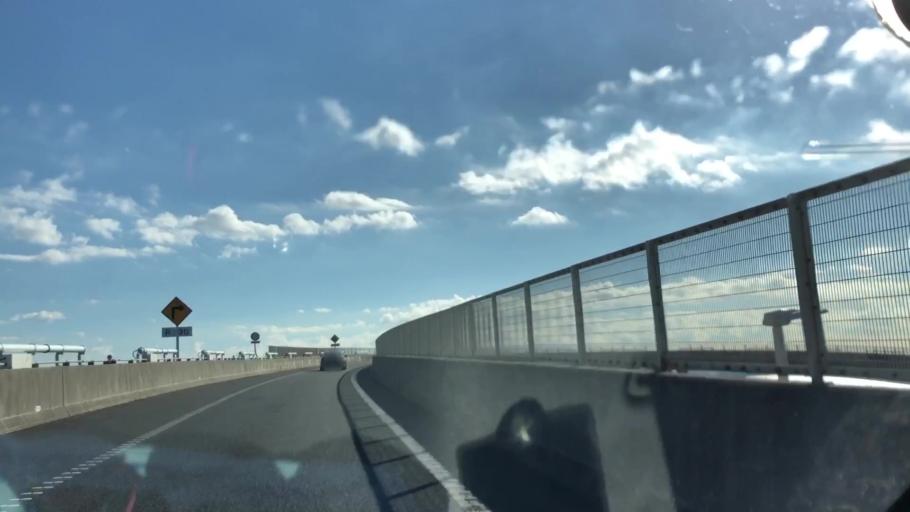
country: JP
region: Chiba
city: Kisarazu
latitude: 35.4626
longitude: 139.8777
